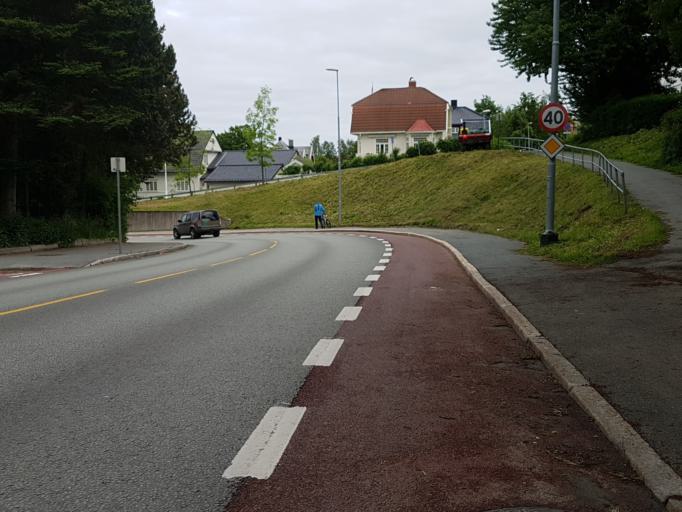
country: NO
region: Sor-Trondelag
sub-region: Trondheim
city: Trondheim
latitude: 63.4338
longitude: 10.4288
